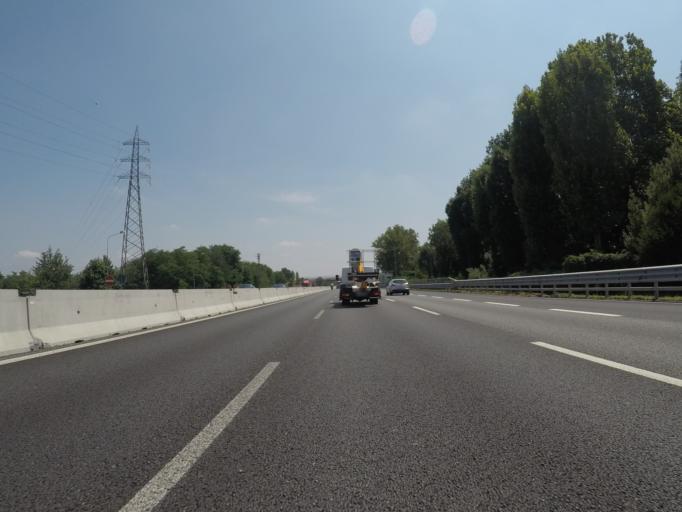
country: IT
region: Lombardy
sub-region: Citta metropolitana di Milano
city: Cerro Maggiore
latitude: 45.6039
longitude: 8.9431
